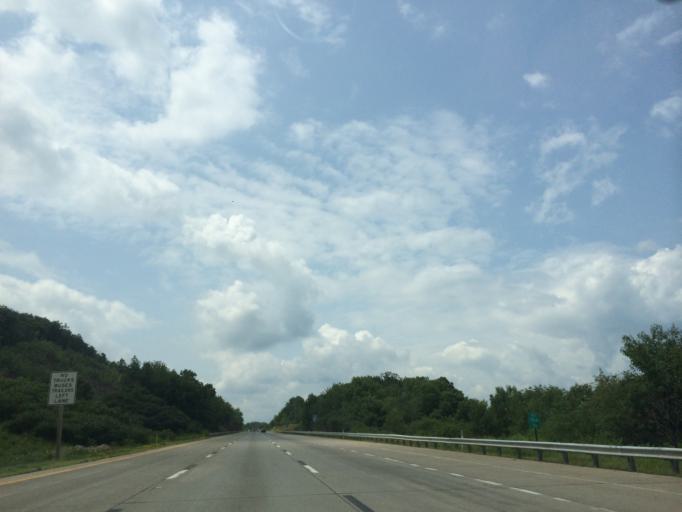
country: US
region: Pennsylvania
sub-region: Luzerne County
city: Freeland
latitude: 41.0770
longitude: -75.9708
